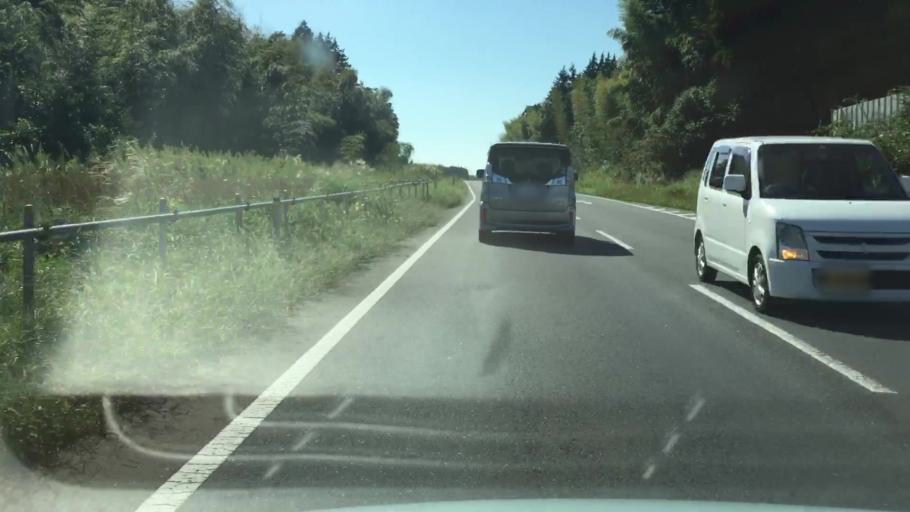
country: JP
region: Ibaraki
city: Ami
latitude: 35.9898
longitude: 140.1849
